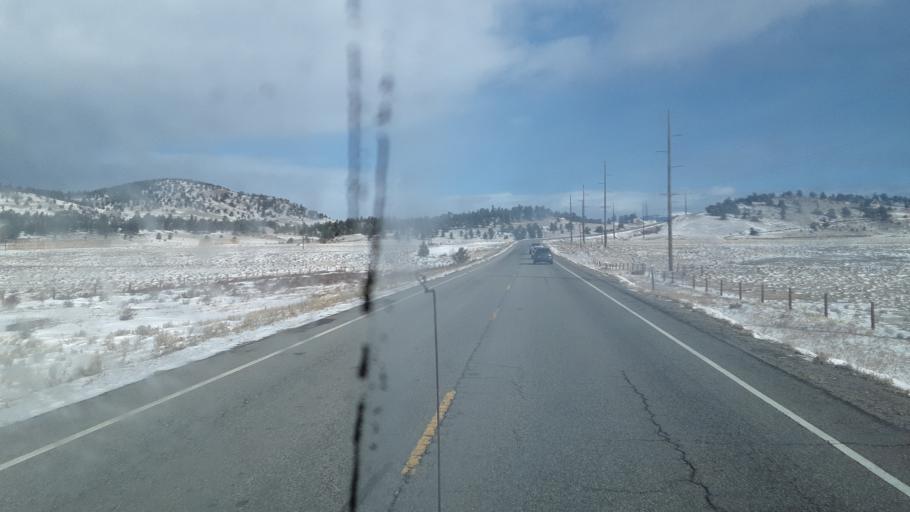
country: US
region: Colorado
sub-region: Park County
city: Fairplay
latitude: 39.2938
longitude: -105.9044
